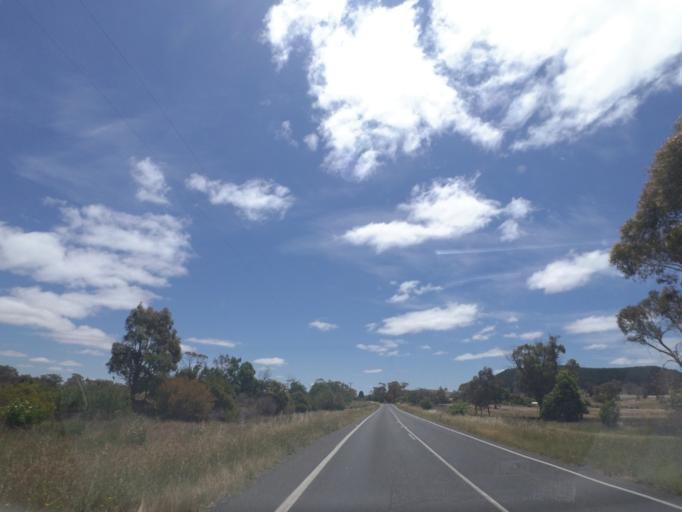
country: AU
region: Victoria
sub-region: Mount Alexander
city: Castlemaine
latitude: -37.2801
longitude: 144.1508
